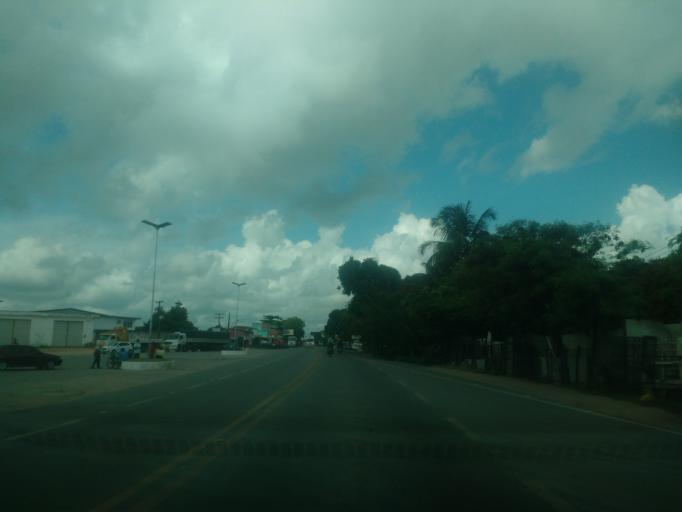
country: BR
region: Alagoas
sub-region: Satuba
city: Satuba
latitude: -9.5649
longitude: -35.7894
